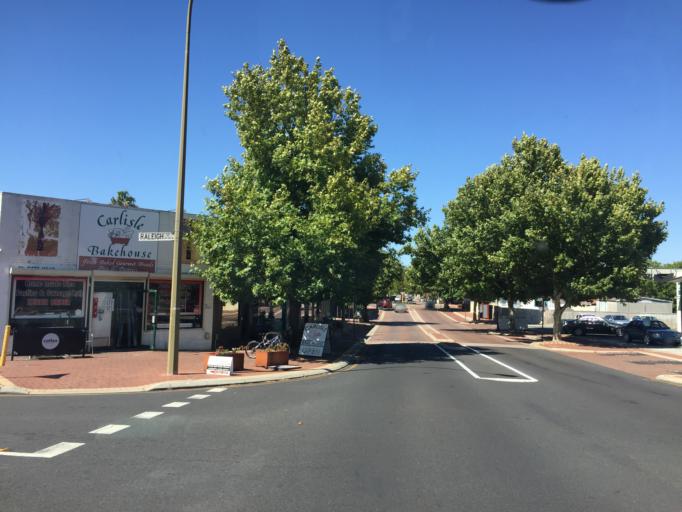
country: AU
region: Western Australia
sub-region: Victoria Park
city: Victoria Park
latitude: -31.9783
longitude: 115.9110
